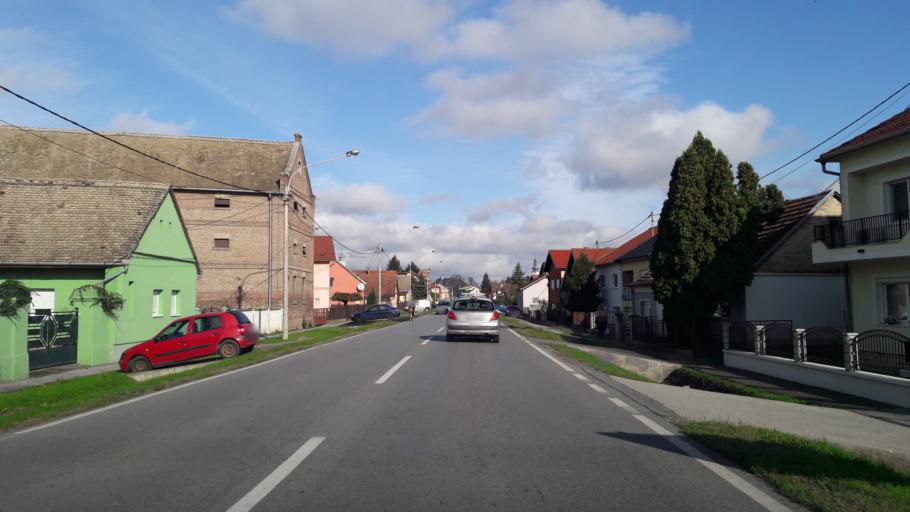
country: HR
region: Osjecko-Baranjska
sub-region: Grad Osijek
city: Bilje
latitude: 45.5992
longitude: 18.7429
